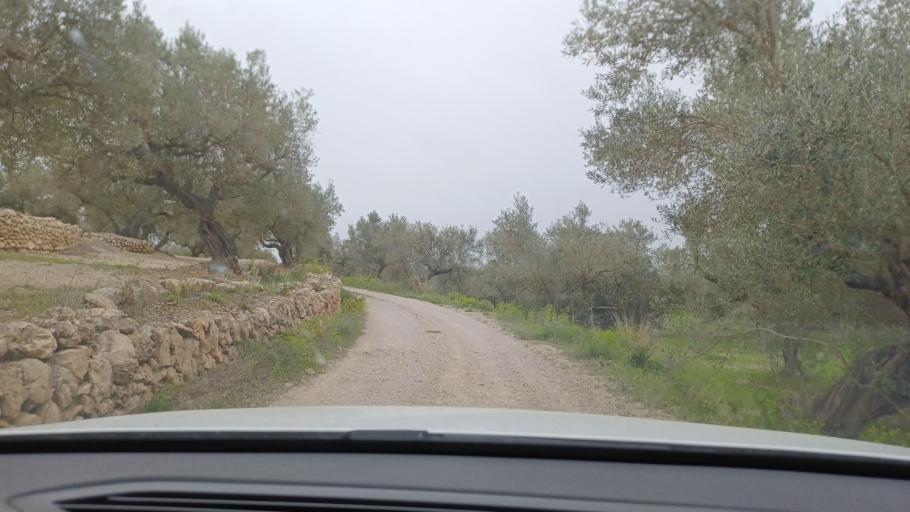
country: ES
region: Catalonia
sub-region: Provincia de Tarragona
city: Mas de Barberans
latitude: 40.8053
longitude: 0.4074
